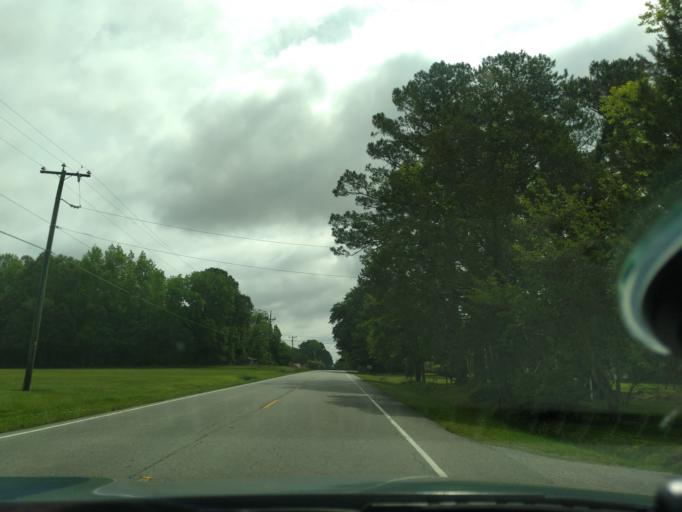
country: US
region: North Carolina
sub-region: Washington County
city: Plymouth
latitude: 35.8739
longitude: -76.6770
